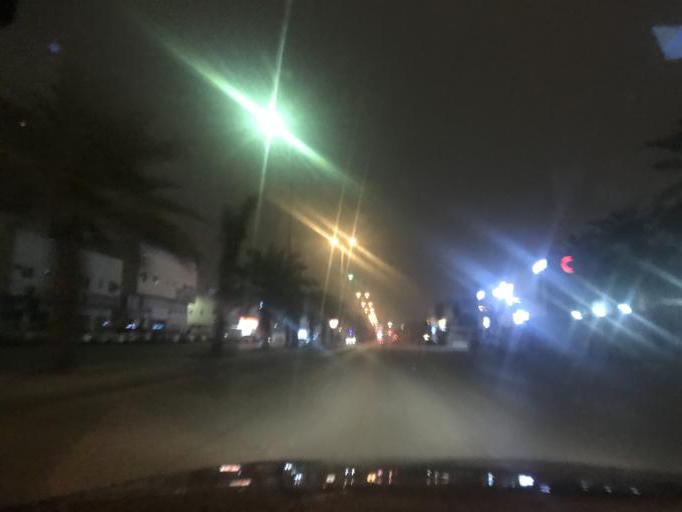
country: SA
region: Ar Riyad
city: Riyadh
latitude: 24.7502
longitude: 46.7795
